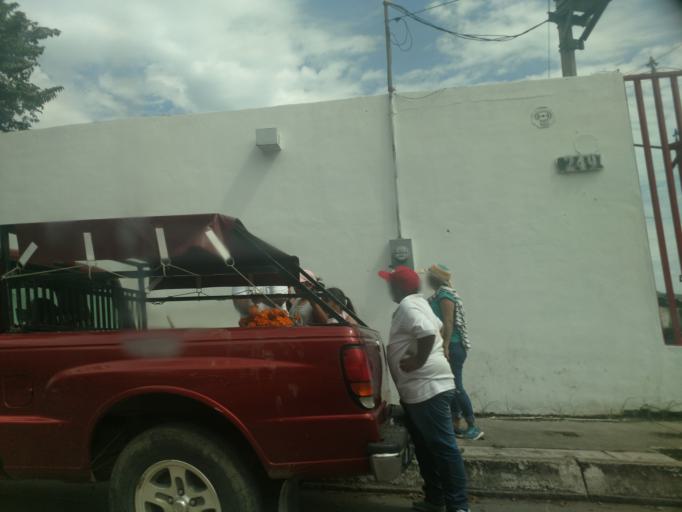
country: MX
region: Nayarit
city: Tepic
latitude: 21.4991
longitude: -104.8816
